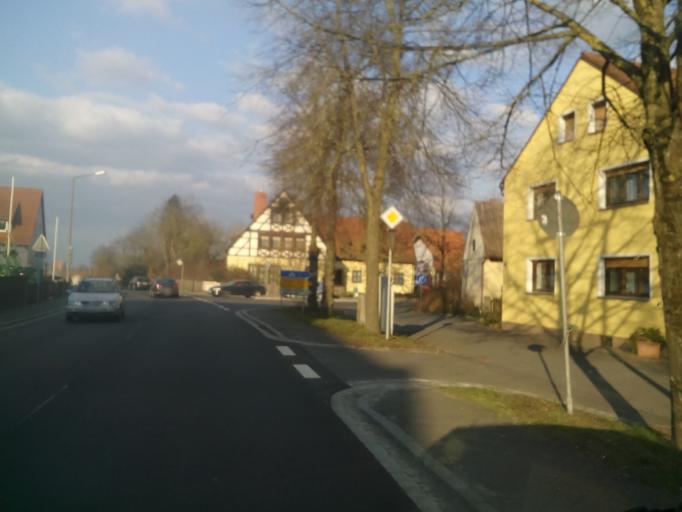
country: DE
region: Bavaria
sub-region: Regierungsbezirk Mittelfranken
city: Gerhardshofen
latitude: 49.6309
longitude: 10.6919
